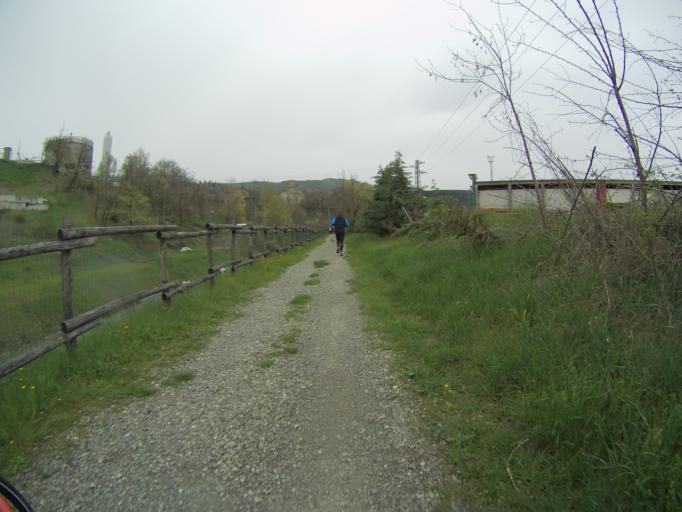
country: IT
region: Emilia-Romagna
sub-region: Provincia di Reggio Emilia
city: Ciano d'Enza
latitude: 44.5973
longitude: 10.4061
